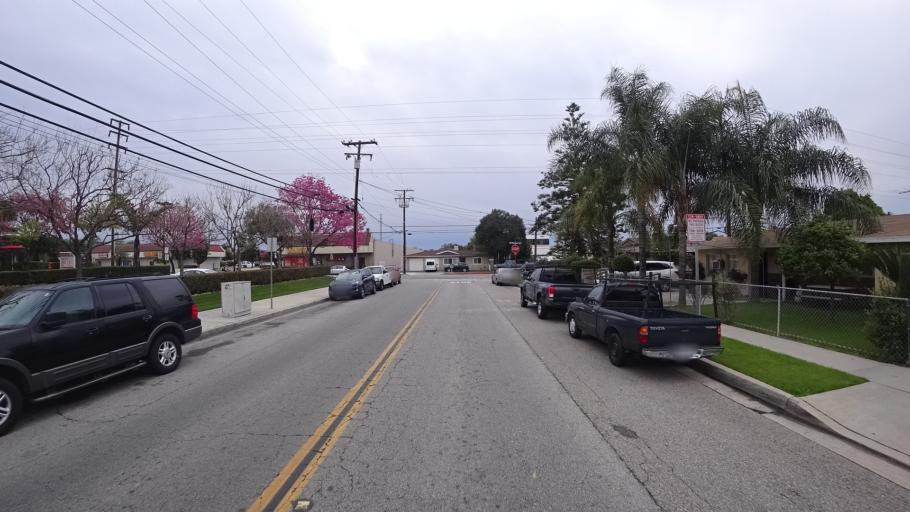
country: US
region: California
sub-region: Los Angeles County
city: West Puente Valley
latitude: 34.0674
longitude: -117.9742
